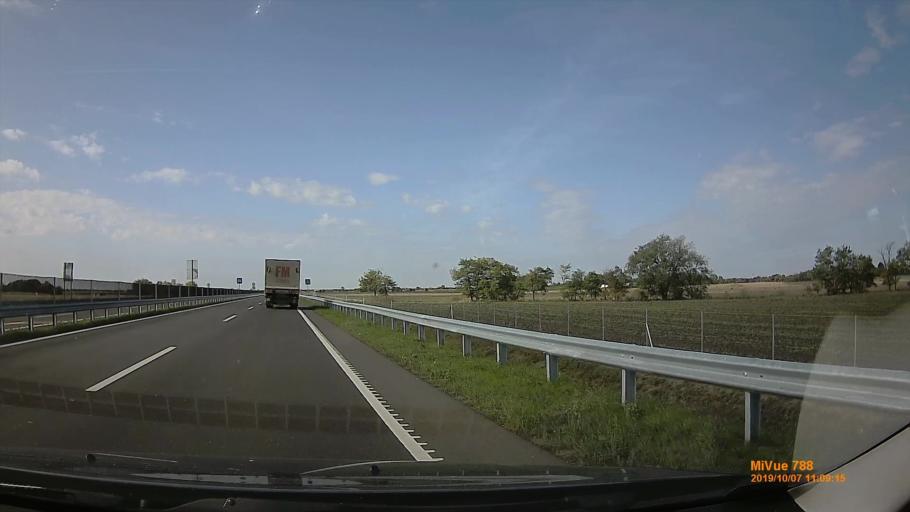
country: HU
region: Bekes
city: Kondoros
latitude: 46.7442
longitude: 20.8372
